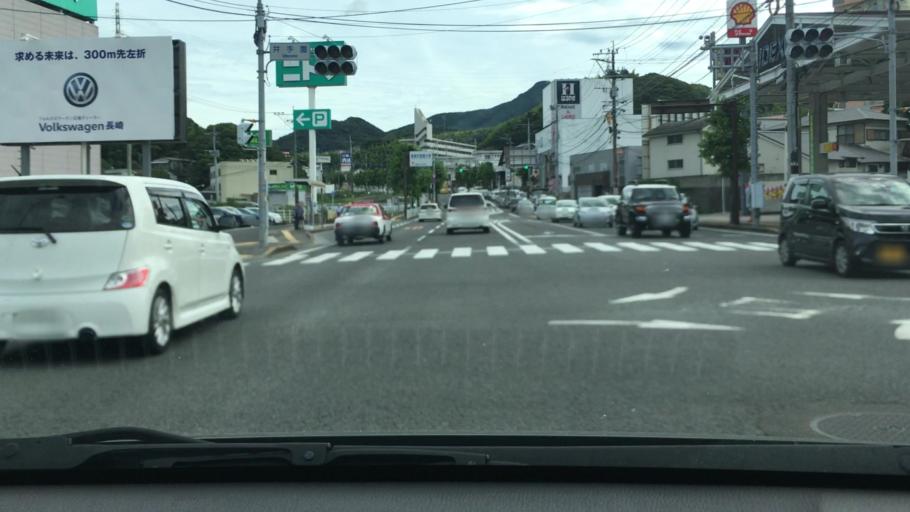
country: JP
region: Nagasaki
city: Togitsu
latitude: 32.8195
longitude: 129.8474
